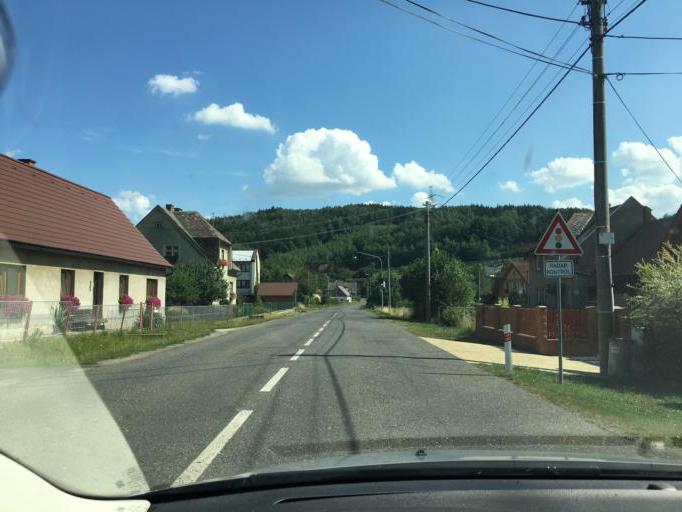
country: CZ
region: Liberecky
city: Hodkovice nad Mohelkou
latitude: 50.6554
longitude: 15.1061
